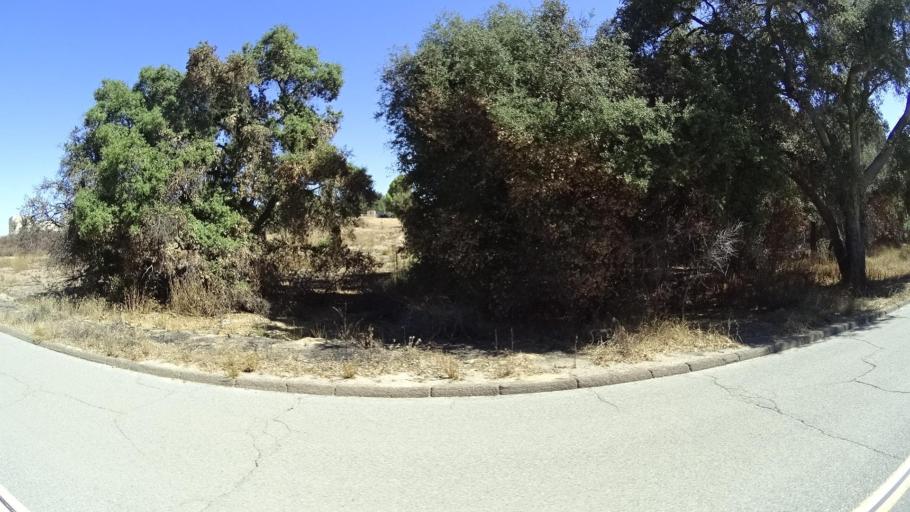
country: US
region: California
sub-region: San Diego County
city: Alpine
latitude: 32.7445
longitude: -116.7546
